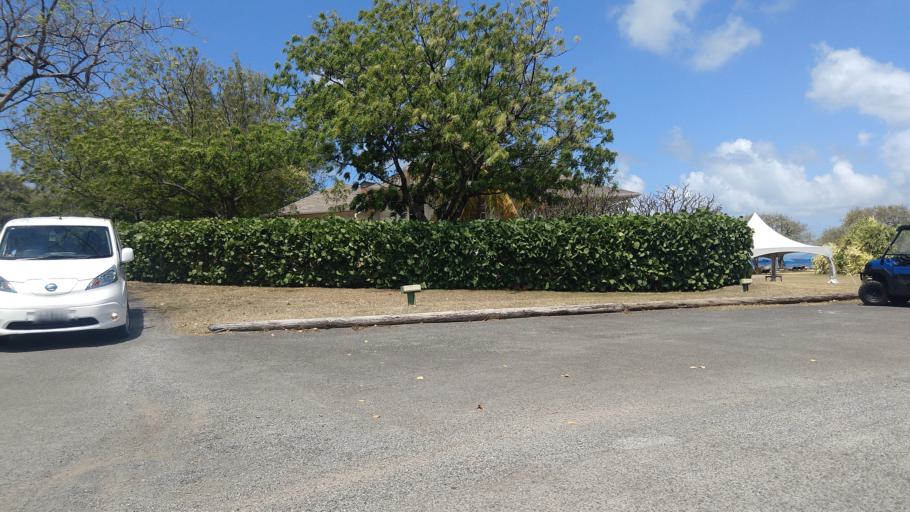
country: VC
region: Grenadines
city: Port Elizabeth
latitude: 12.8889
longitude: -61.1845
